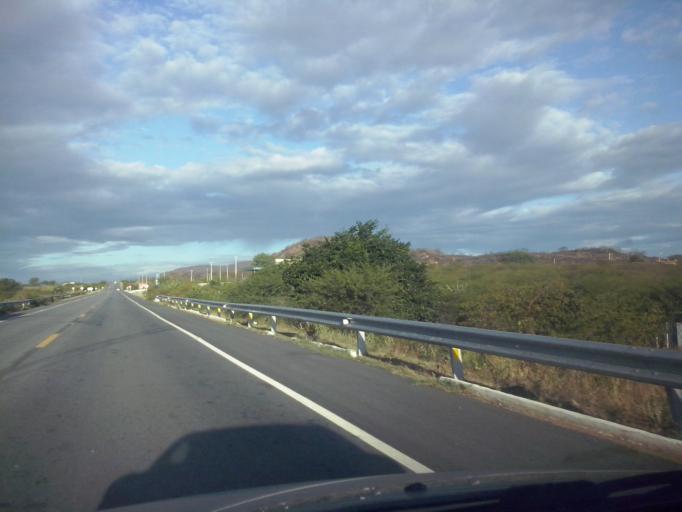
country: BR
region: Paraiba
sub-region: Patos
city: Patos
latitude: -6.9069
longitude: -37.5103
